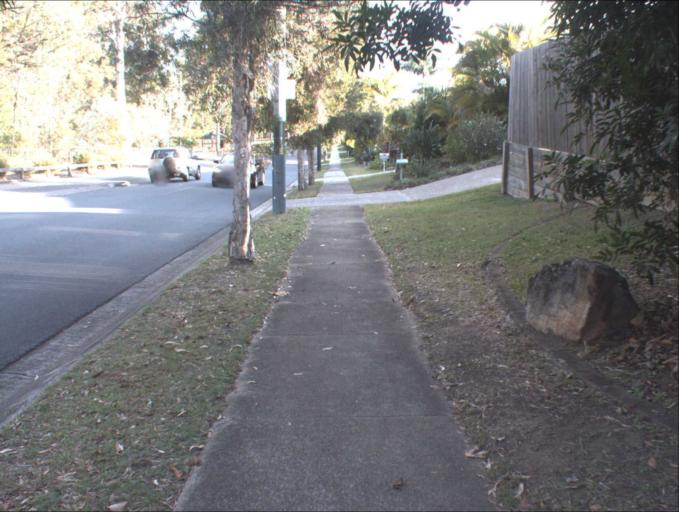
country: AU
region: Queensland
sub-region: Logan
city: Springwood
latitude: -27.6288
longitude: 153.1374
